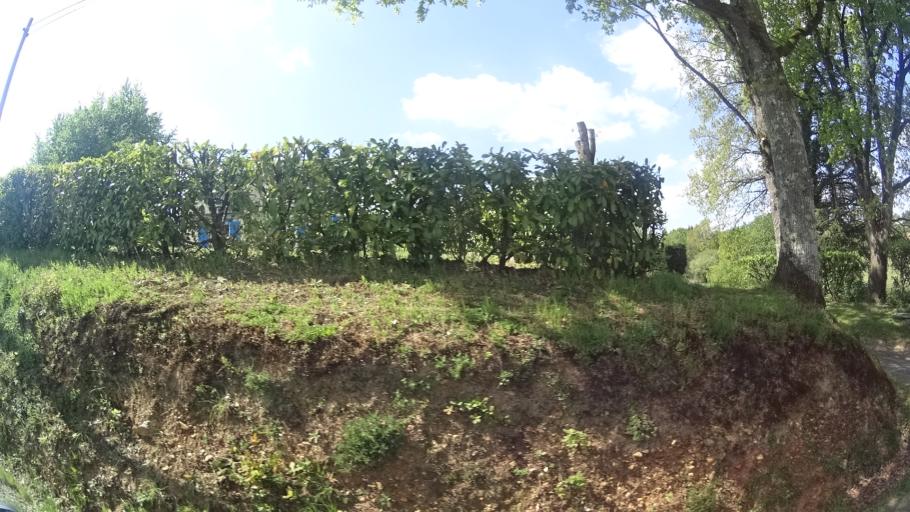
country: FR
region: Brittany
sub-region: Departement du Morbihan
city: Beganne
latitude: 47.5889
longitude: -2.2413
